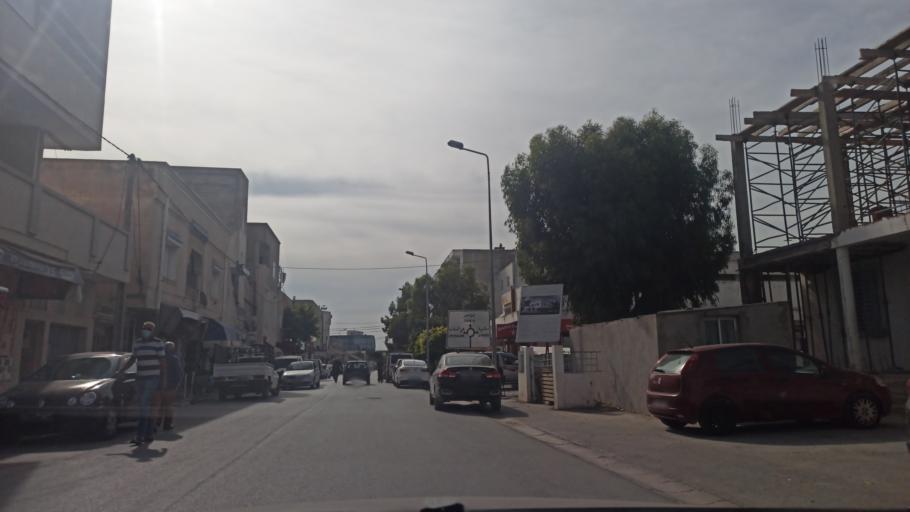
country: TN
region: Tunis
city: La Goulette
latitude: 36.8506
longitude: 10.2628
